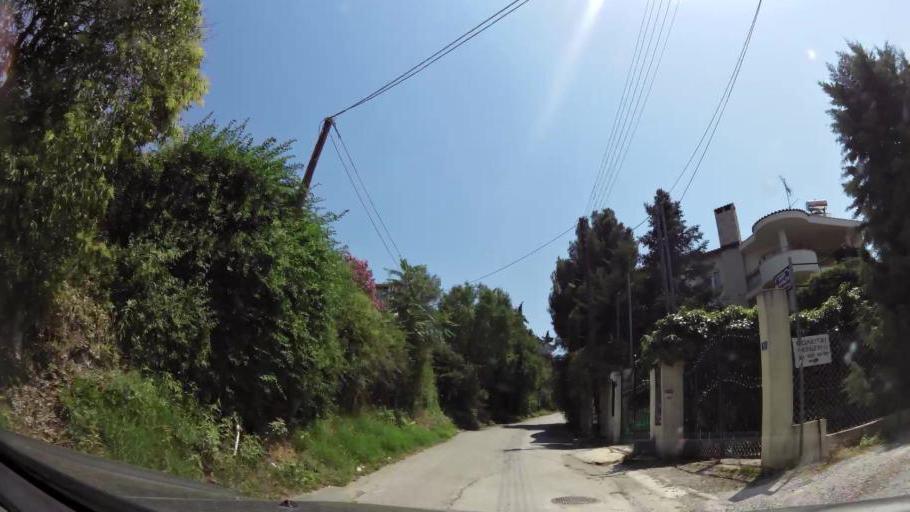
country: GR
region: Central Macedonia
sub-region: Nomos Thessalonikis
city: Trilofos
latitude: 40.4638
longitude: 22.9749
